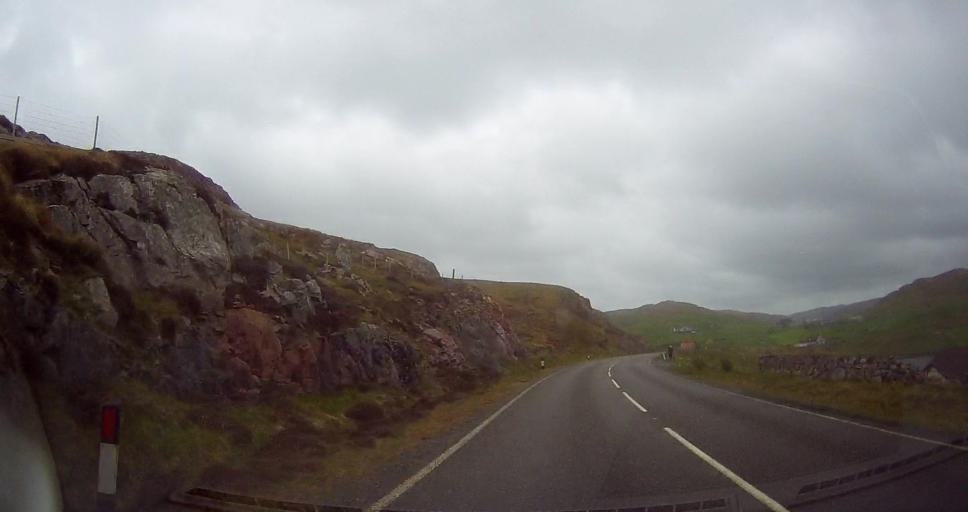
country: GB
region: Scotland
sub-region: Shetland Islands
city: Lerwick
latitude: 60.4114
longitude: -1.3900
